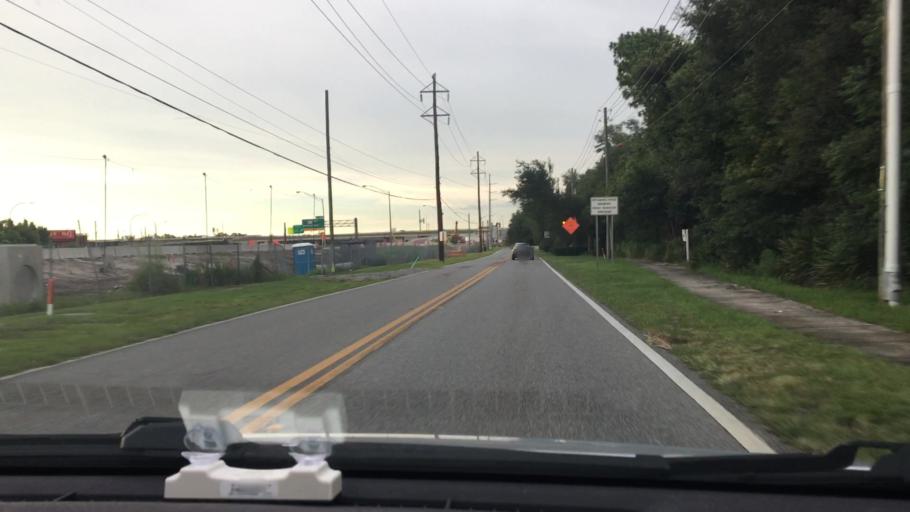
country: US
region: Florida
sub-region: Orange County
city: Eatonville
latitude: 28.6257
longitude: -81.3860
